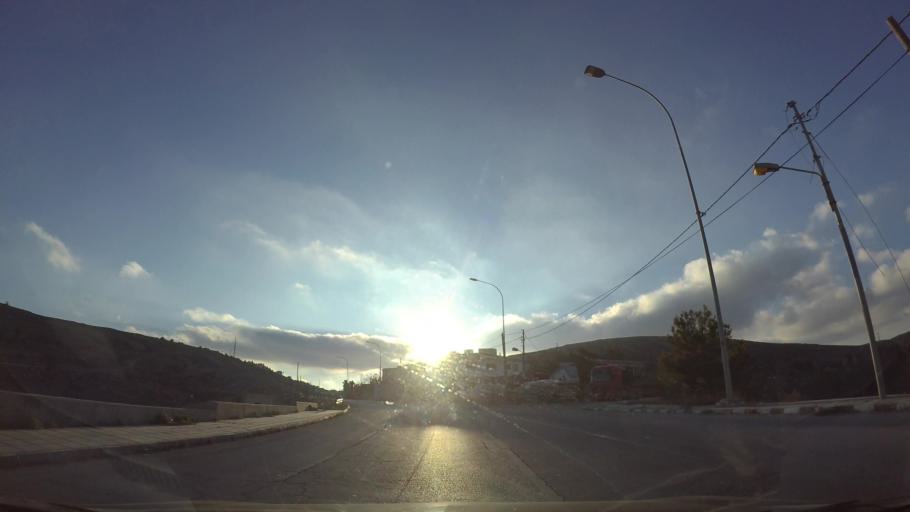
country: JO
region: Ma'an
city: Petra
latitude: 30.5218
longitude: 35.5499
